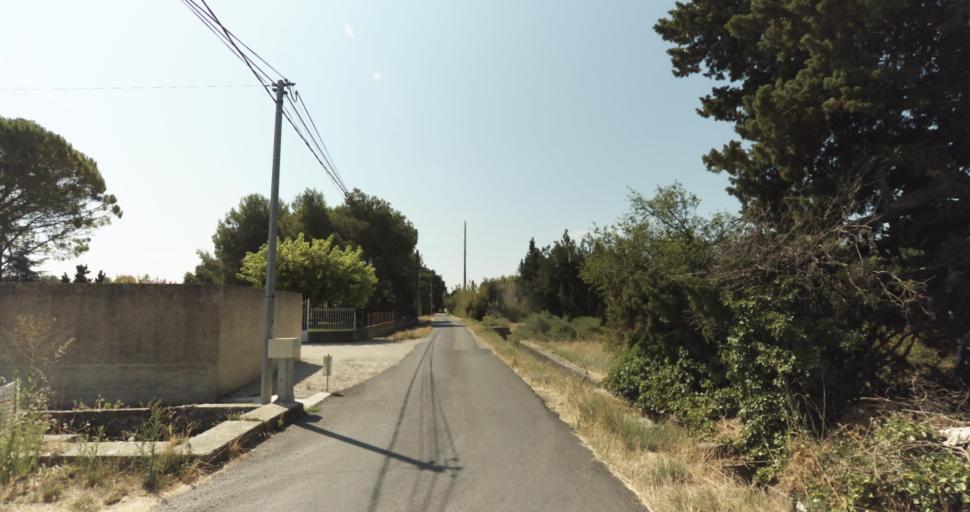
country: FR
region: Provence-Alpes-Cote d'Azur
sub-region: Departement du Vaucluse
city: Monteux
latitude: 44.0257
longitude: 5.0089
